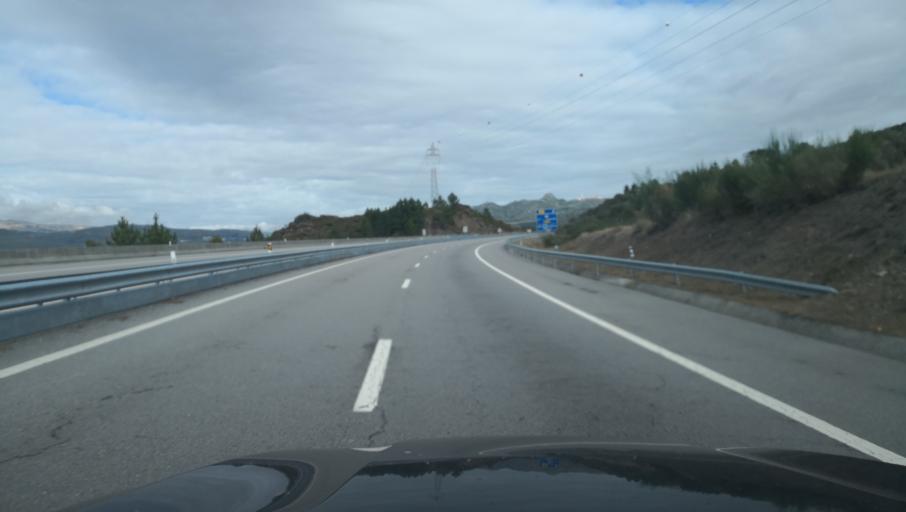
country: PT
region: Vila Real
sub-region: Vila Real
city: Vila Real
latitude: 41.3433
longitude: -7.7055
